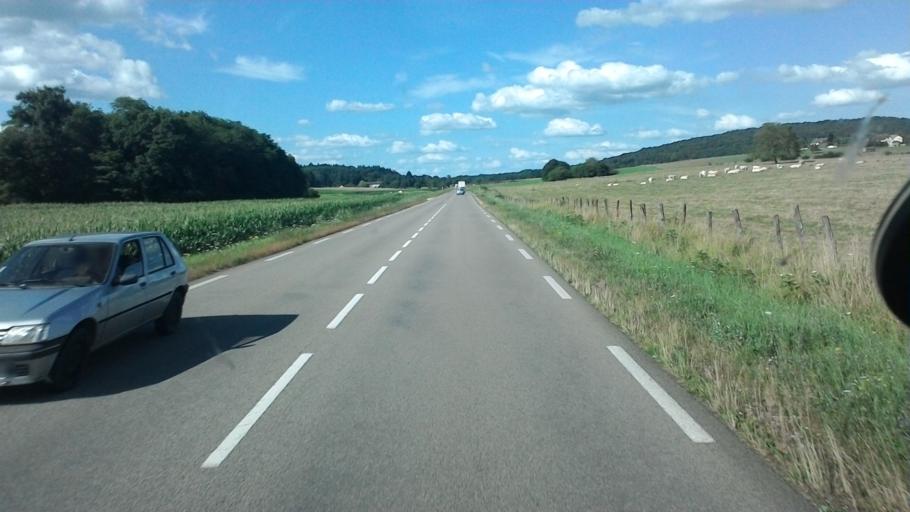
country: FR
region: Franche-Comte
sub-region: Departement de la Haute-Saone
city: Noidans-les-Vesoul
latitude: 47.5798
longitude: 6.0936
